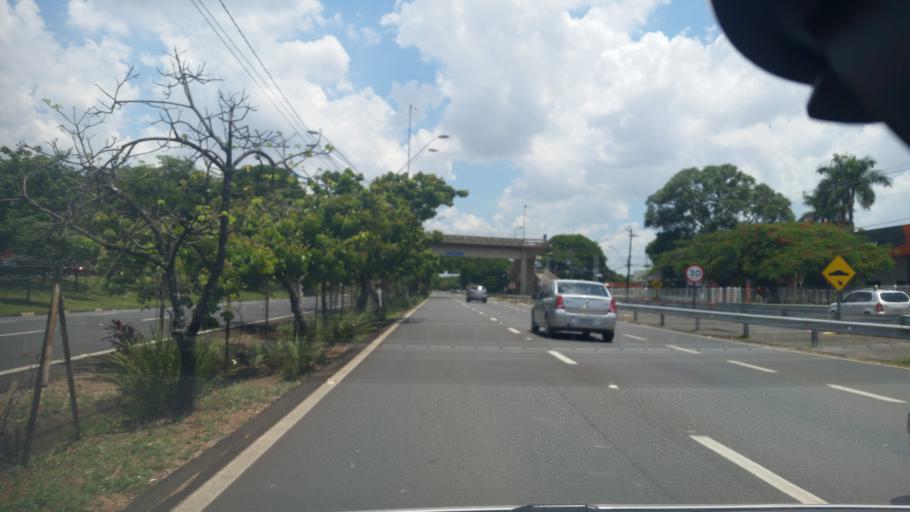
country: BR
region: Sao Paulo
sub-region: Campinas
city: Campinas
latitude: -22.8608
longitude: -47.0439
